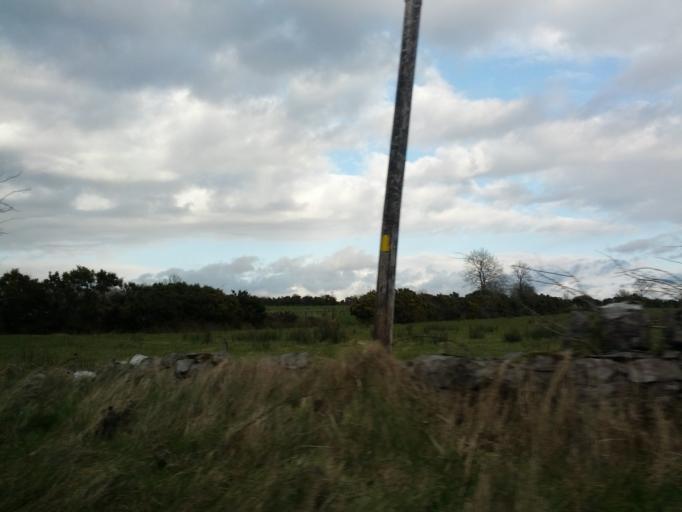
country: IE
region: Connaught
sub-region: County Galway
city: Athenry
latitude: 53.4107
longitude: -8.5850
